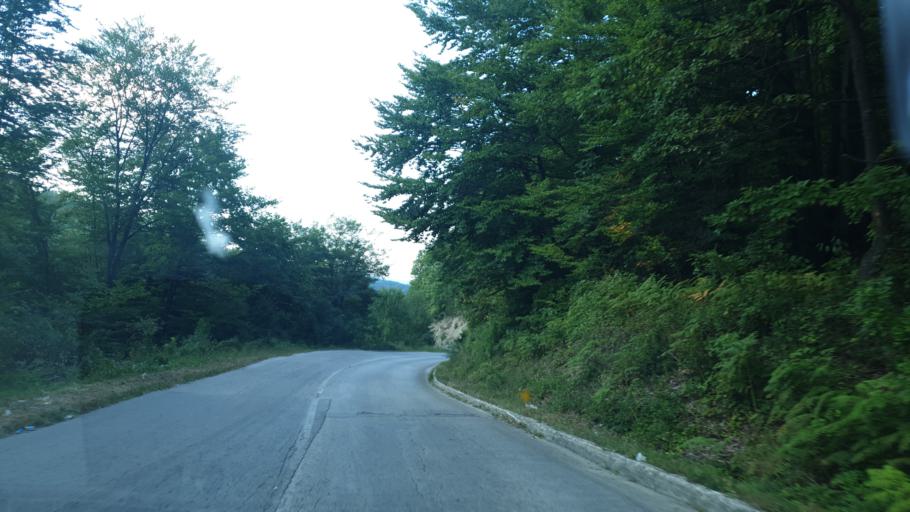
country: RS
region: Central Serbia
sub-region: Zlatiborski Okrug
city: Uzice
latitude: 43.8660
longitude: 19.9061
